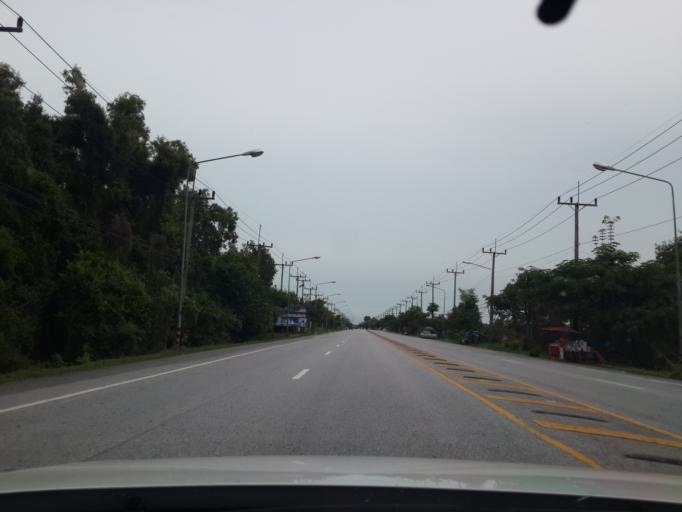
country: TH
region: Pattani
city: Nong Chik
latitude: 6.8098
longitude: 101.1554
